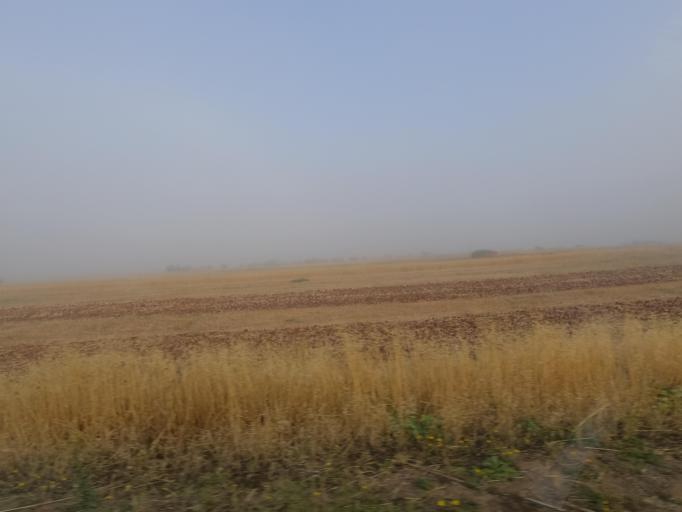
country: CY
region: Ammochostos
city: Achna
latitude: 35.0505
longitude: 33.7925
